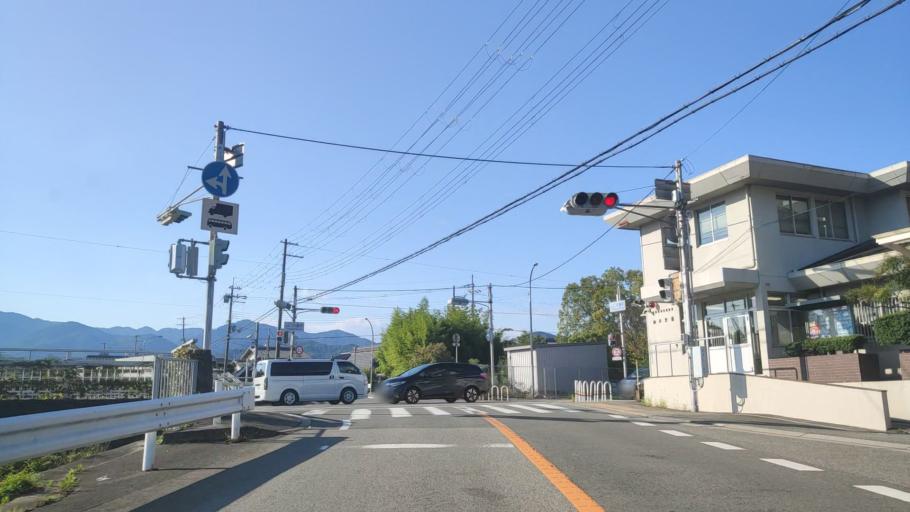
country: JP
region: Hyogo
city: Sandacho
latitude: 34.8282
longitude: 135.2408
